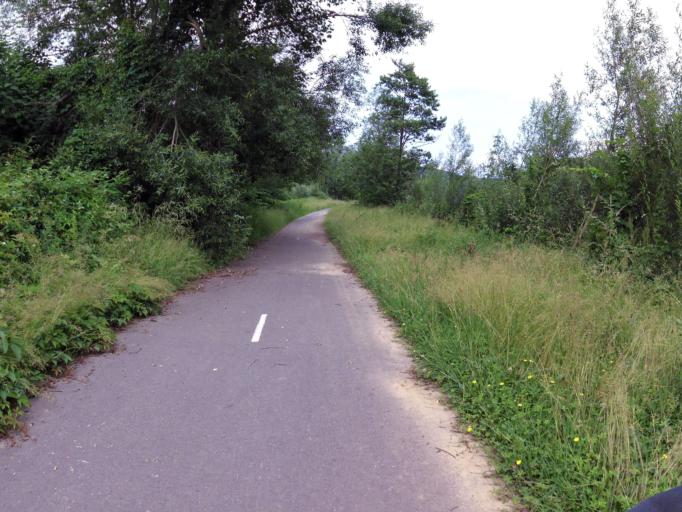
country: FR
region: Champagne-Ardenne
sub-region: Departement des Ardennes
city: Nouzonville
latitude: 49.8232
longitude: 4.7441
